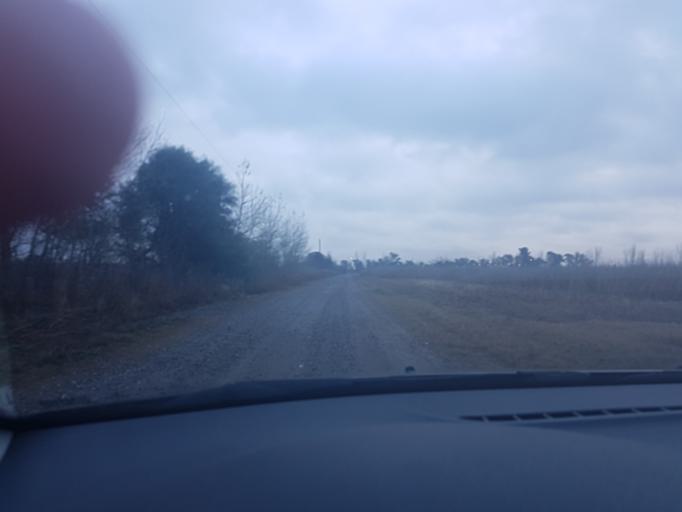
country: AR
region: Cordoba
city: Villa Allende
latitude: -31.3076
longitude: -64.2256
